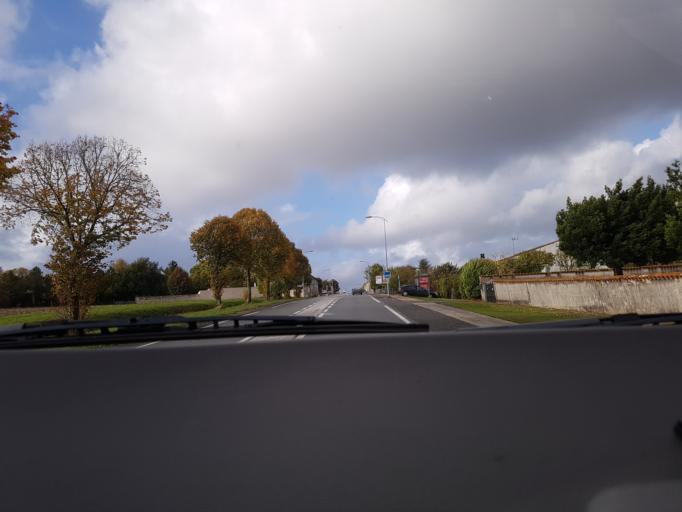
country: FR
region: Poitou-Charentes
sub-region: Departement de la Charente-Maritime
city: Thenac
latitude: 45.6509
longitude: -0.5861
